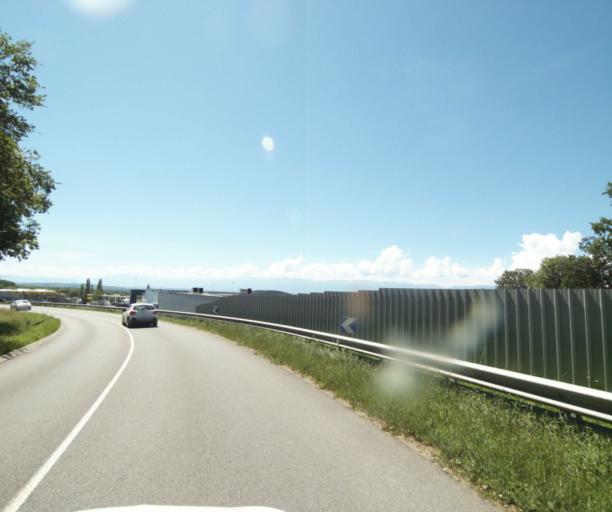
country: FR
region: Rhone-Alpes
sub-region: Departement de la Haute-Savoie
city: Loisin
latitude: 46.2693
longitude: 6.3181
